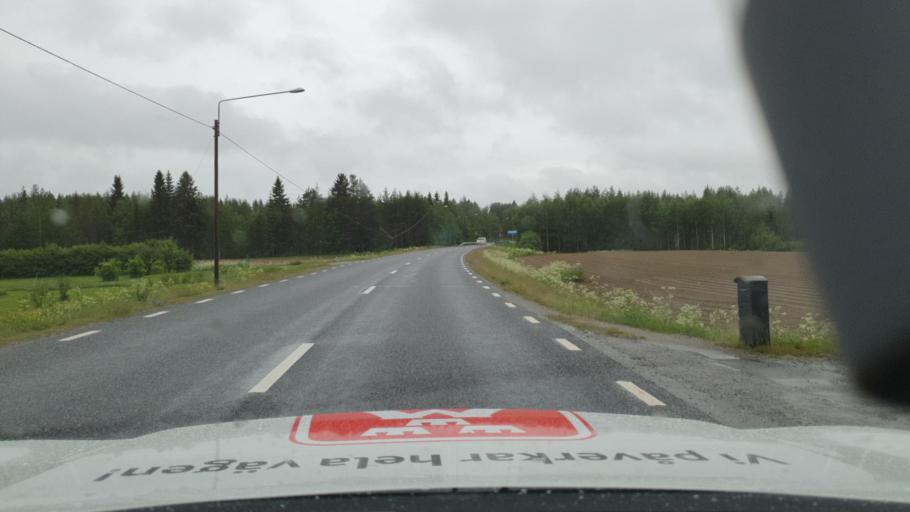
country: SE
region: Vaesterbotten
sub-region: Asele Kommun
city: Asele
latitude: 64.0116
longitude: 17.2900
